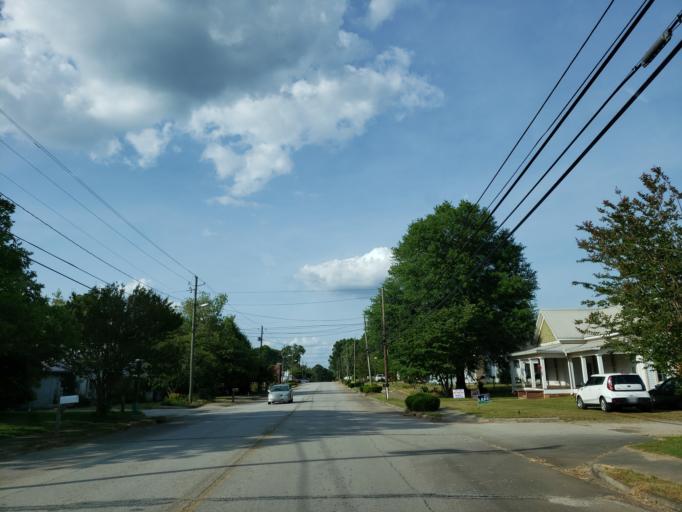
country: US
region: Georgia
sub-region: Carroll County
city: Carrollton
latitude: 33.4547
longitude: -85.1318
